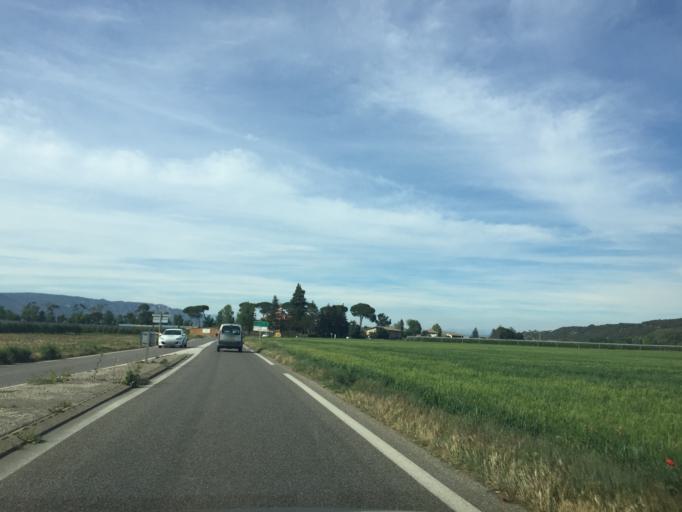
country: FR
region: Provence-Alpes-Cote d'Azur
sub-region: Departement des Alpes-de-Haute-Provence
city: Manosque
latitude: 43.7966
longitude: 5.8307
